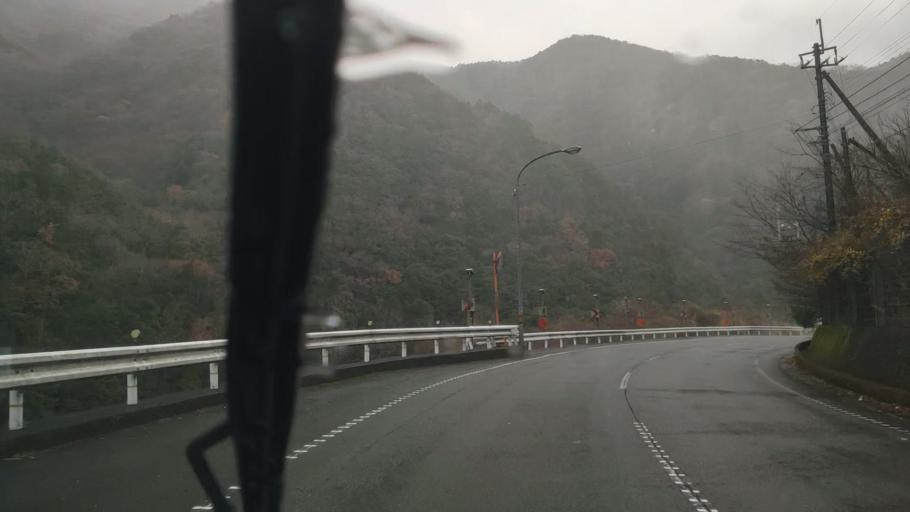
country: JP
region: Tokushima
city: Kamojimacho-jogejima
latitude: 34.1473
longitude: 134.3545
